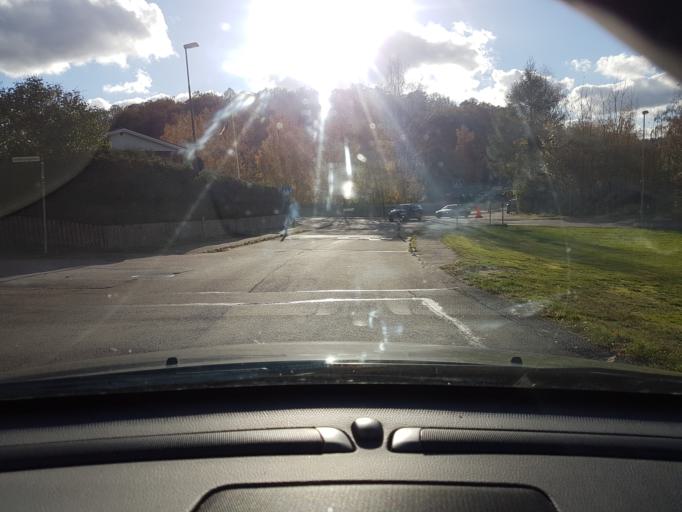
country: SE
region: Vaestra Goetaland
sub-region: Ale Kommun
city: Surte
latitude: 57.8298
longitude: 12.0205
